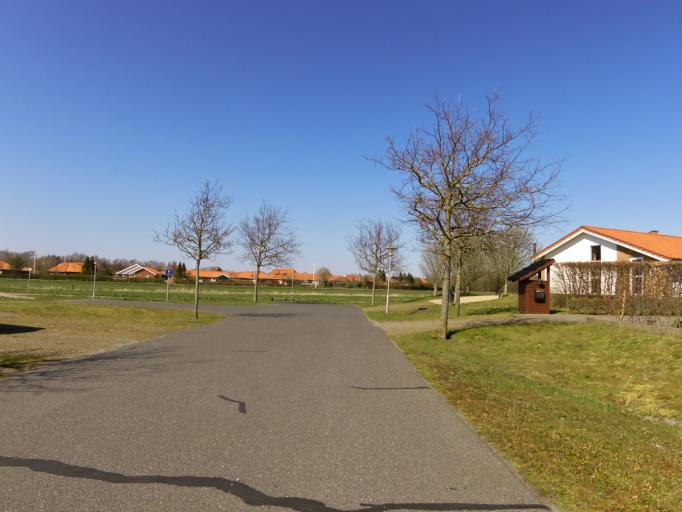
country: DK
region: South Denmark
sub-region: Esbjerg Kommune
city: Ribe
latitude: 55.3375
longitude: 8.7886
